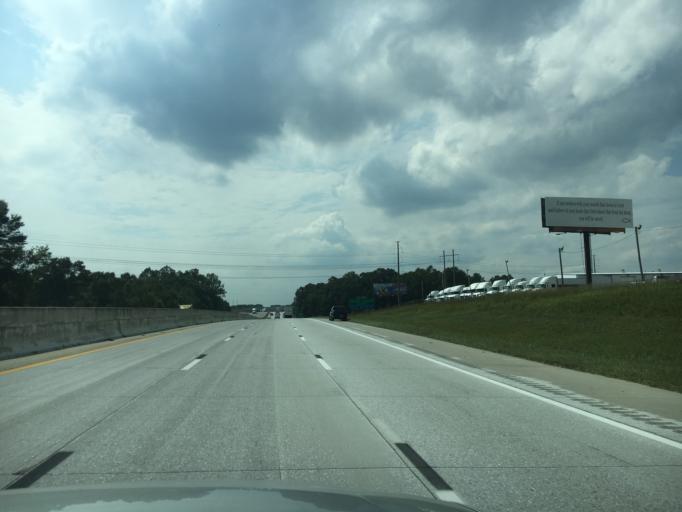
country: US
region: South Carolina
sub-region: Anderson County
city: Williamston
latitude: 34.6356
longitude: -82.5907
